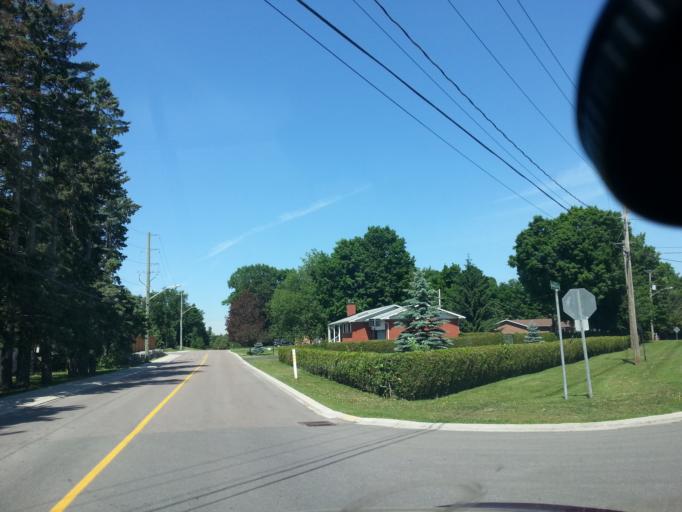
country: CA
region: Ontario
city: Carleton Place
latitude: 45.1453
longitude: -76.1559
